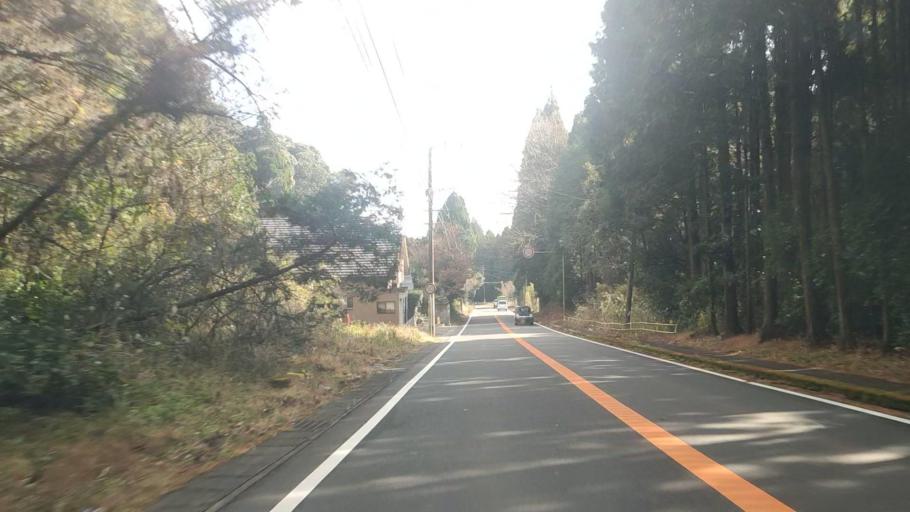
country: JP
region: Kagoshima
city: Kajiki
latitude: 31.8255
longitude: 130.6902
